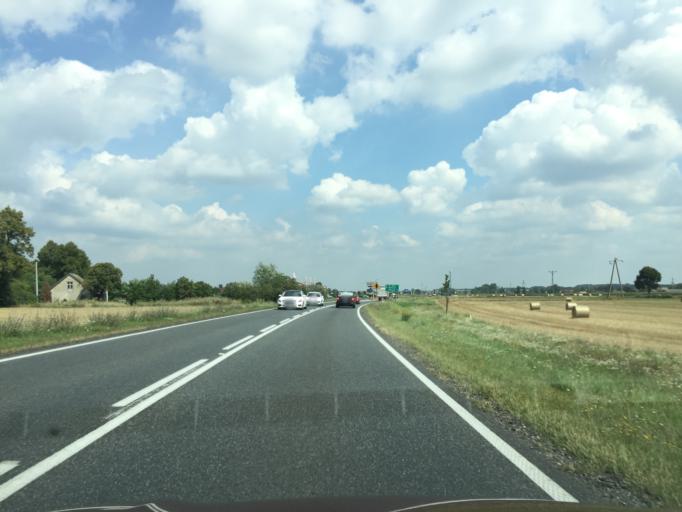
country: PL
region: Greater Poland Voivodeship
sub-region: Powiat kaliski
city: Stawiszyn
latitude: 51.9078
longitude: 18.1060
